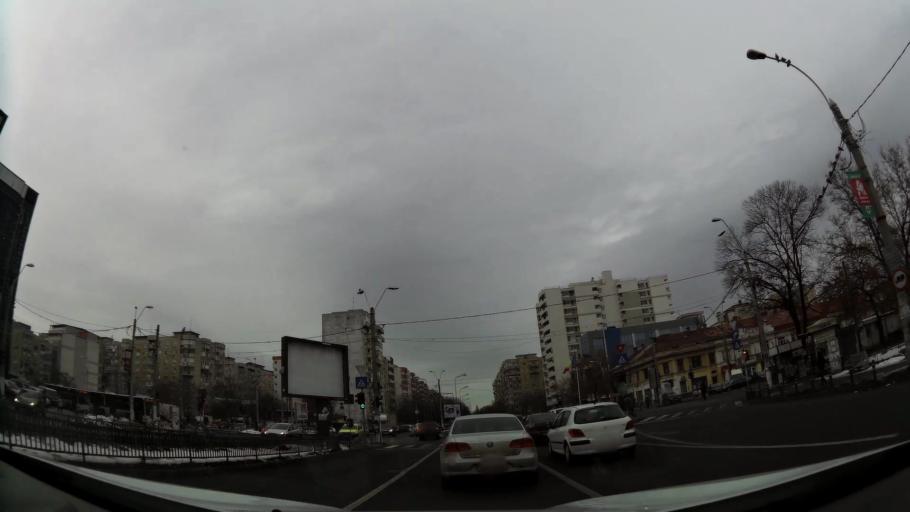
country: RO
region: Bucuresti
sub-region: Municipiul Bucuresti
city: Bucuresti
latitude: 44.4204
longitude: 26.0661
